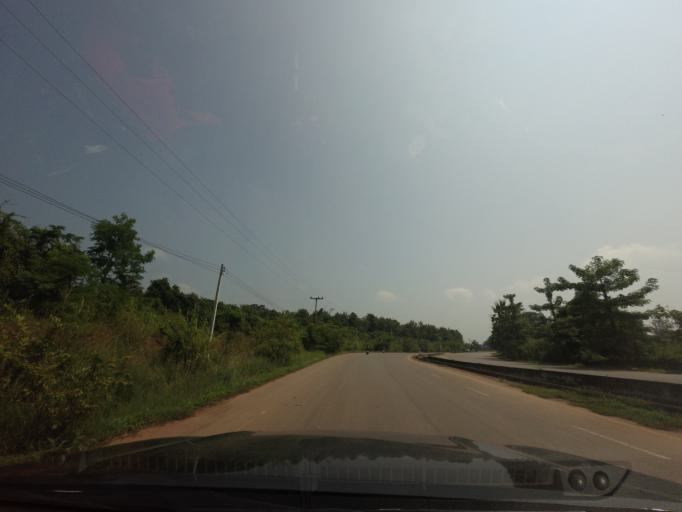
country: TH
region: Nan
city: Nan
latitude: 18.7893
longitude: 100.7489
